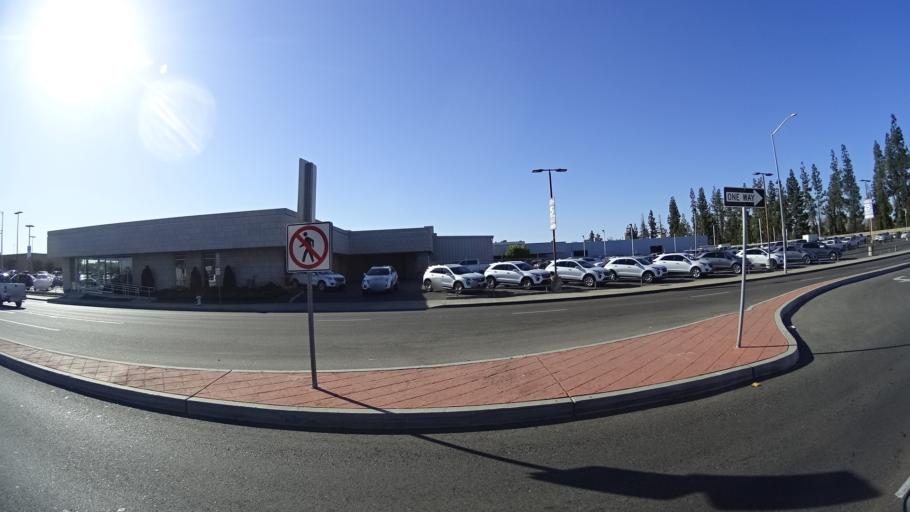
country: US
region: California
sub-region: Fresno County
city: Fresno
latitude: 36.8230
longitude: -119.7914
